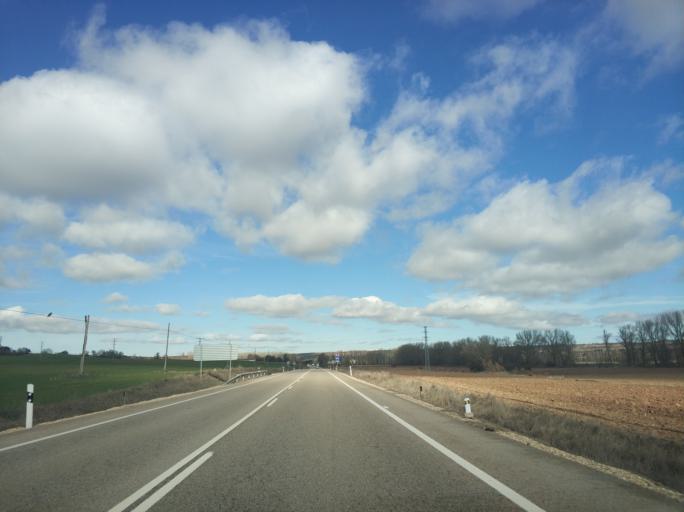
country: ES
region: Castille and Leon
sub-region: Provincia de Burgos
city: Sarracin
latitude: 42.2455
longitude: -3.6788
